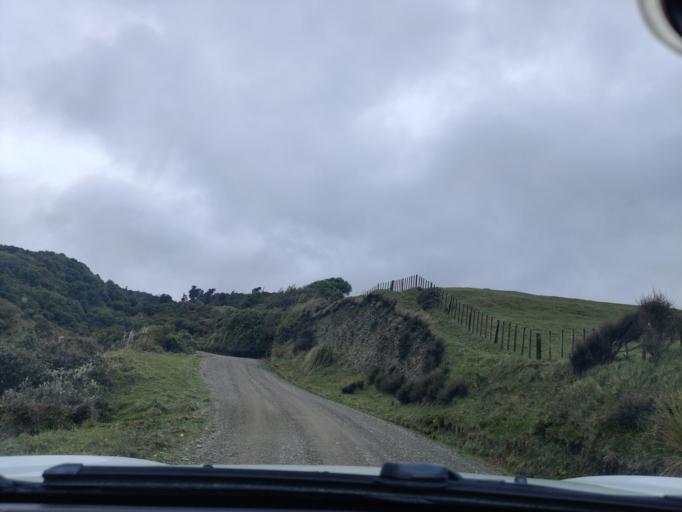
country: NZ
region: Manawatu-Wanganui
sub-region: Palmerston North City
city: Palmerston North
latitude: -40.2742
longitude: 175.8495
